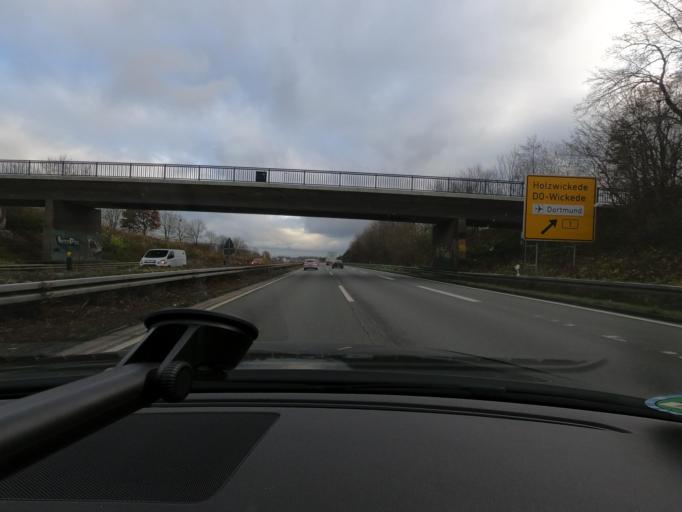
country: DE
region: North Rhine-Westphalia
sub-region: Regierungsbezirk Arnsberg
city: Holzwickede
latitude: 51.5093
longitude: 7.6086
